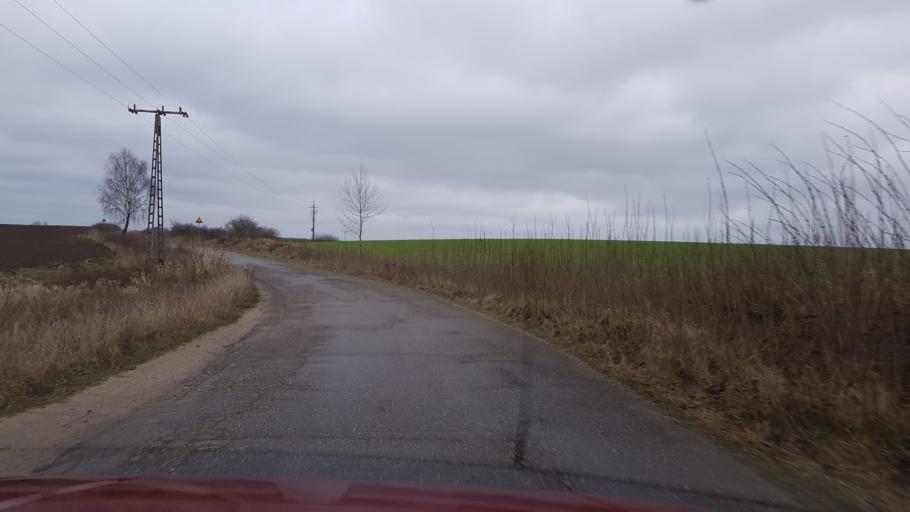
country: PL
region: Pomeranian Voivodeship
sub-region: Powiat bytowski
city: Tuchomie
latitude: 54.1566
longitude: 17.3336
